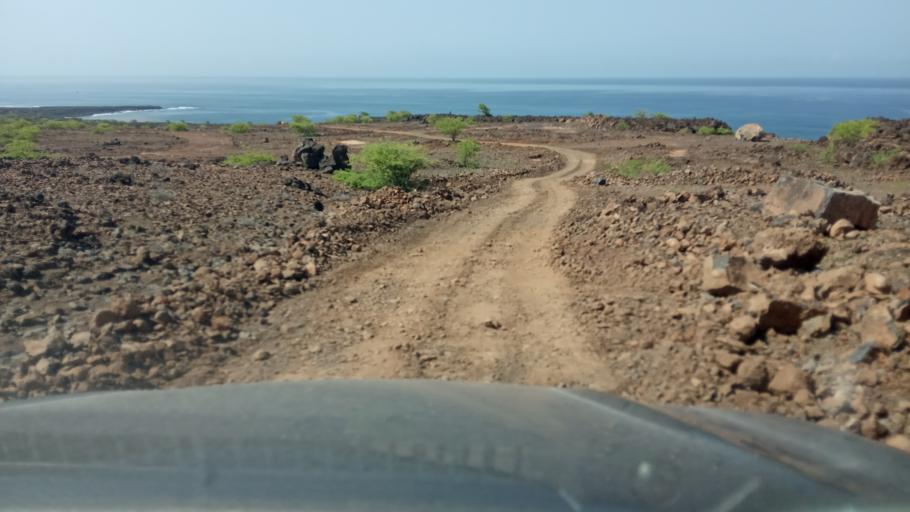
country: CV
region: Porto Novo
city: Porto Novo
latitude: 16.9398
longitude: -25.3158
